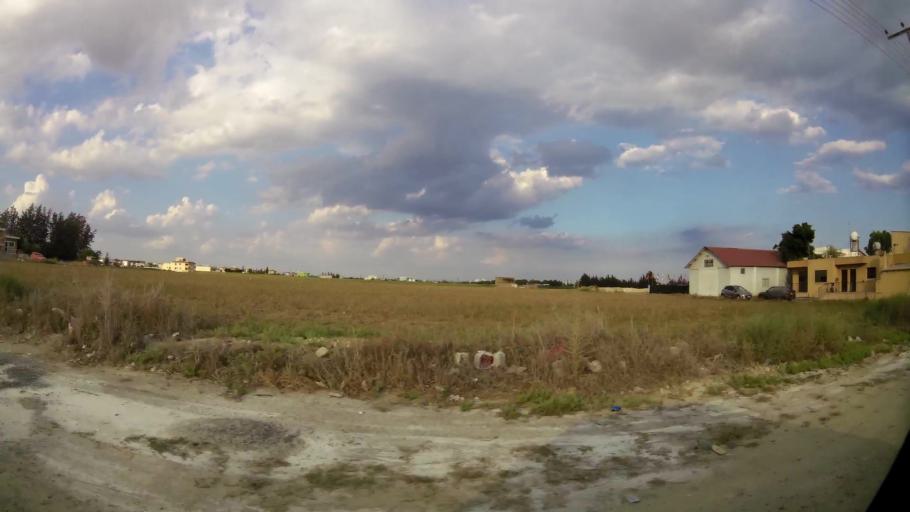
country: CY
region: Larnaka
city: Meneou
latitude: 34.8636
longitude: 33.5932
